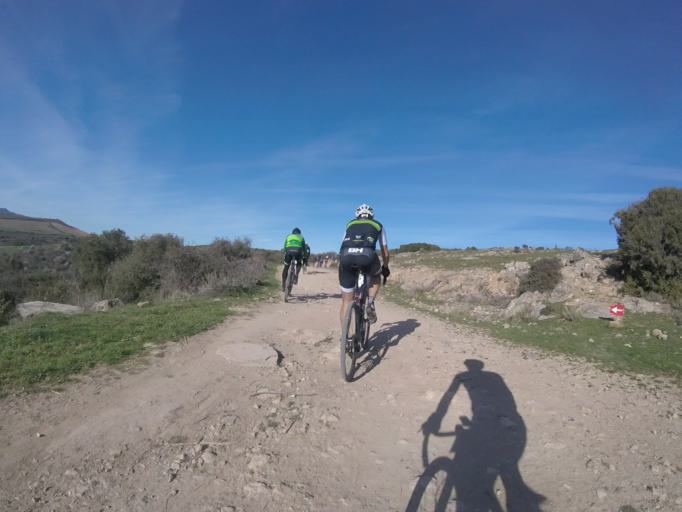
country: ES
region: Navarre
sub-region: Provincia de Navarra
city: Yerri
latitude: 42.6965
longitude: -1.9601
